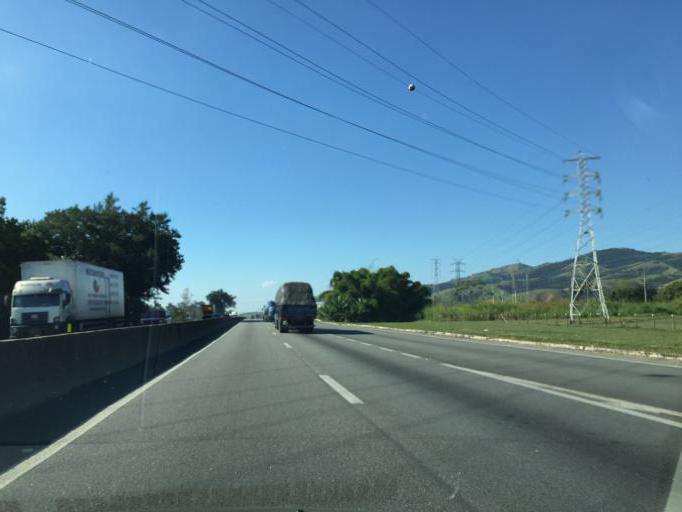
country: BR
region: Sao Paulo
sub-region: Aparecida
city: Aparecida
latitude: -22.9018
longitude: -45.3058
